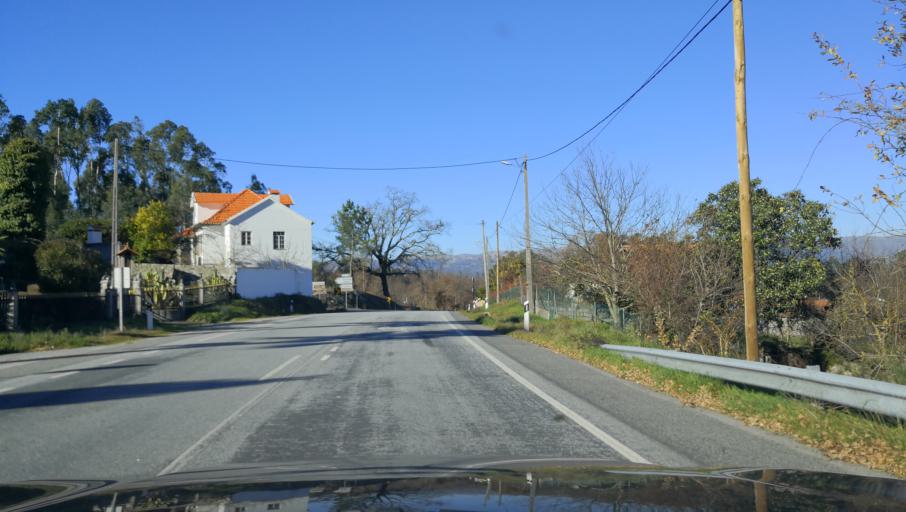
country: PT
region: Viseu
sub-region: Vouzela
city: Vouzela
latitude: 40.7061
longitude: -8.1438
